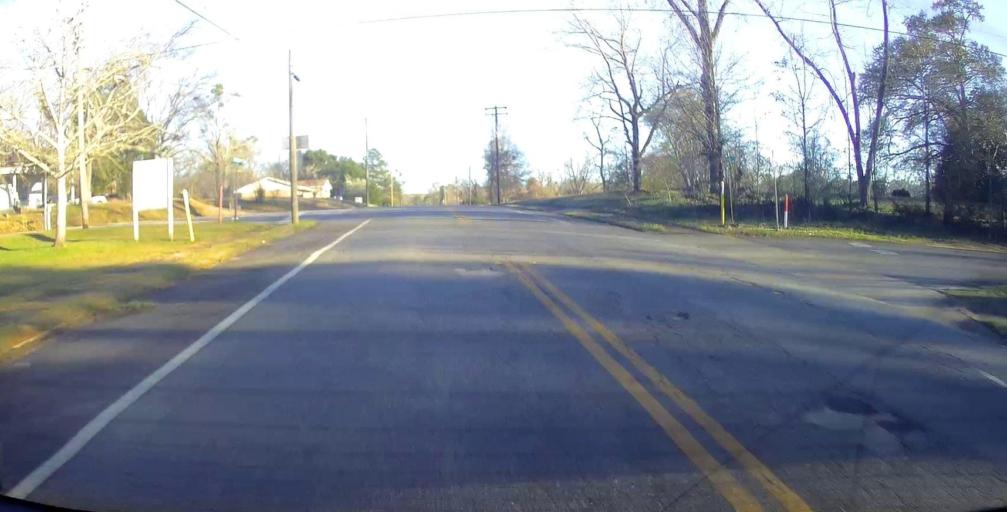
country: US
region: Georgia
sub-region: Talbot County
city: Talbotton
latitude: 32.6732
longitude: -84.5385
